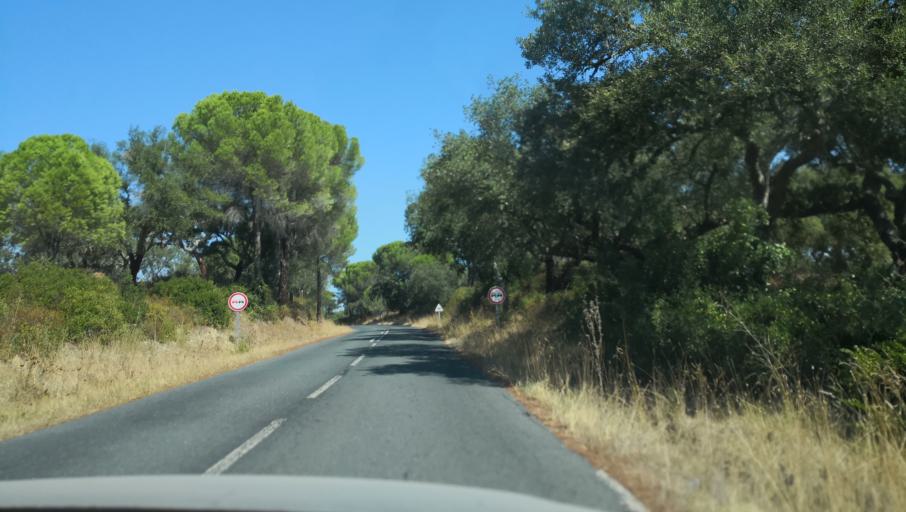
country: PT
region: Setubal
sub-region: Alcacer do Sal
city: Alcacer do Sal
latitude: 38.2968
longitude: -8.4047
